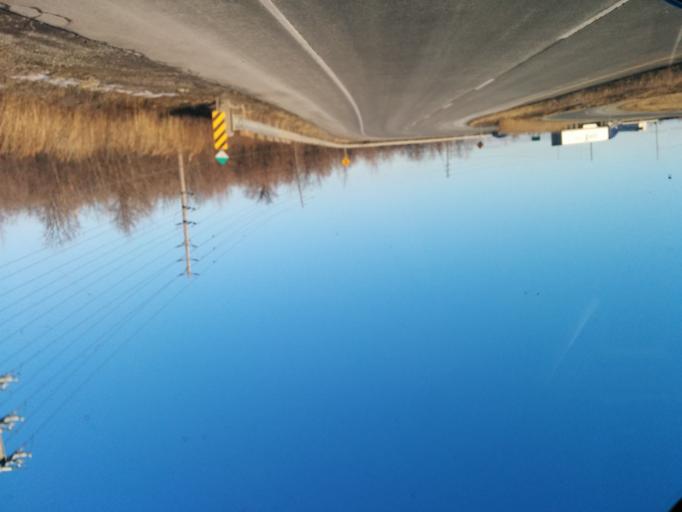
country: CA
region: Ontario
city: Mississauga
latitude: 43.6213
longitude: -79.6338
